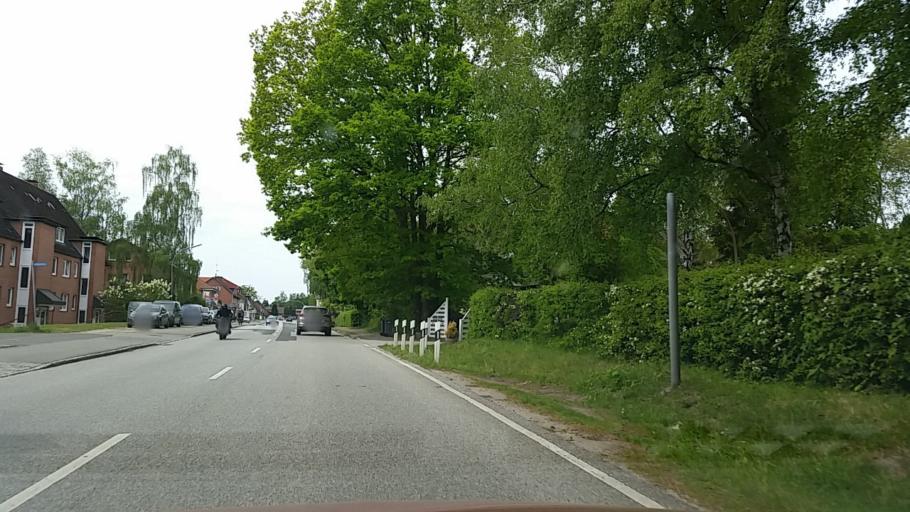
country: DE
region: Schleswig-Holstein
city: Bornsen
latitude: 53.4688
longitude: 10.2816
